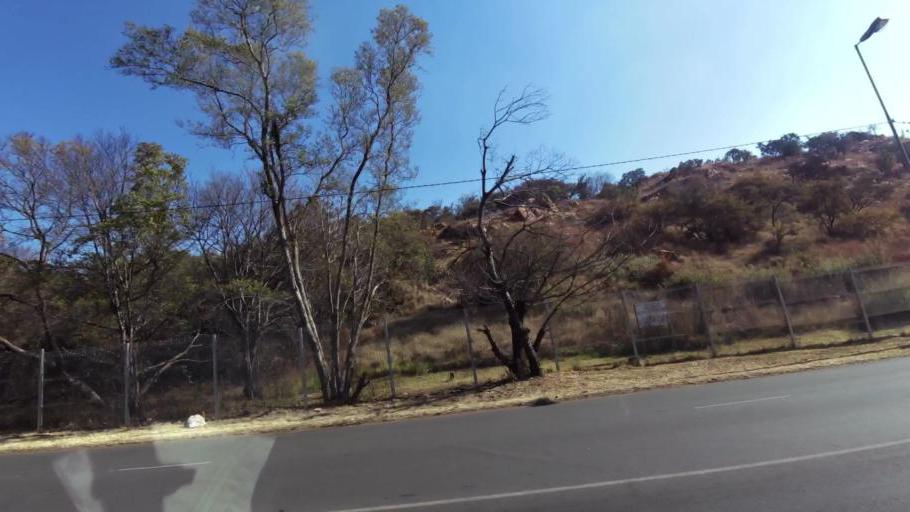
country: ZA
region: Gauteng
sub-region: City of Johannesburg Metropolitan Municipality
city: Johannesburg
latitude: -26.1702
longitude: 27.9984
